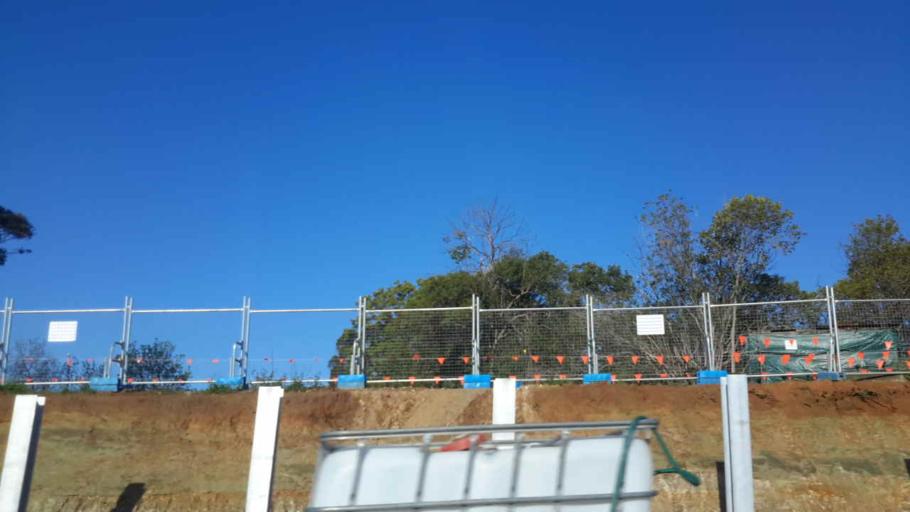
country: AU
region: New South Wales
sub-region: Penrith Municipality
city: Kingswood Park
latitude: -33.7689
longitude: 150.7106
